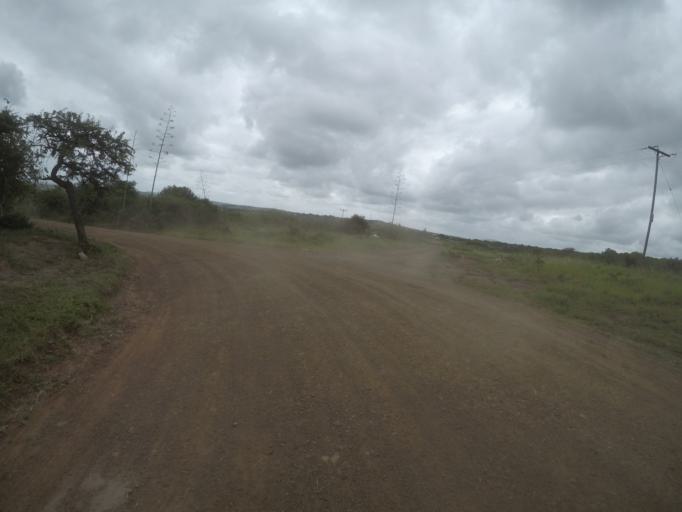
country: ZA
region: KwaZulu-Natal
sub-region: uThungulu District Municipality
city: Empangeni
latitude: -28.5676
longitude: 31.8744
